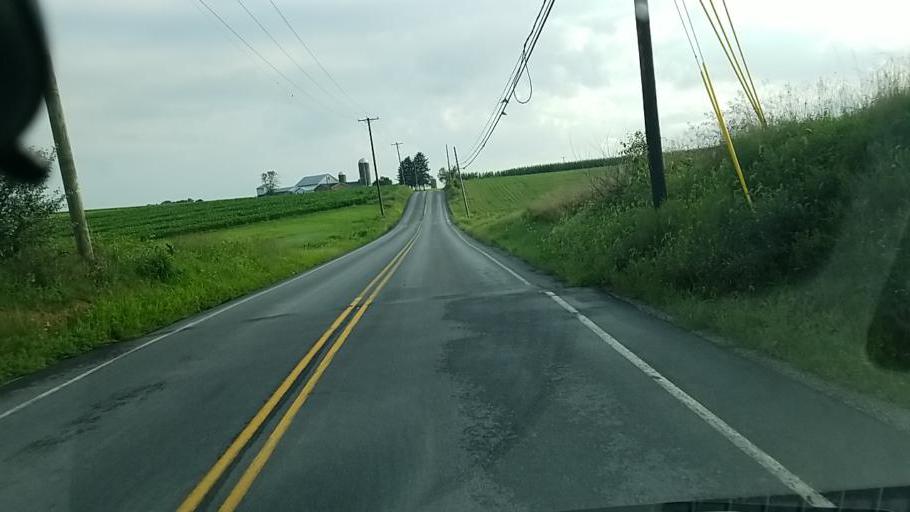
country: US
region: Pennsylvania
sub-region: Cumberland County
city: Shippensburg
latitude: 40.1718
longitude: -77.5458
